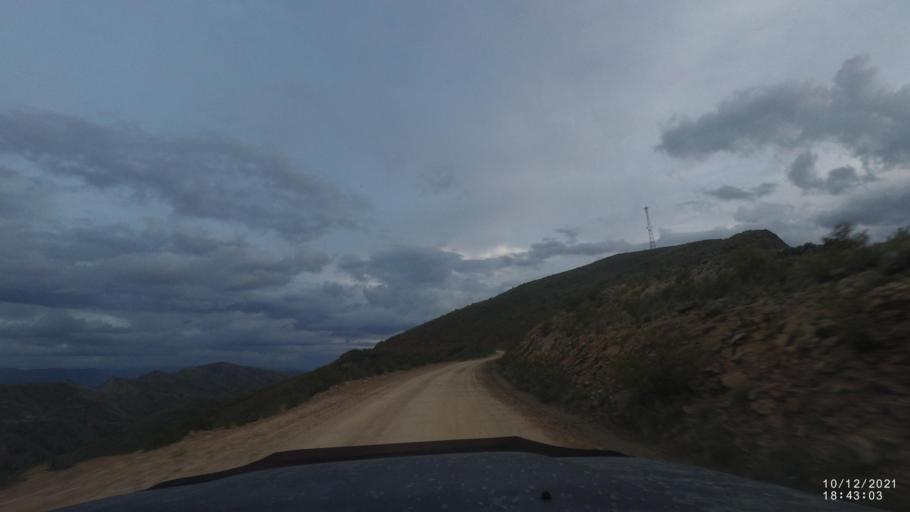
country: BO
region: Cochabamba
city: Tarata
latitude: -17.8740
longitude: -65.9818
